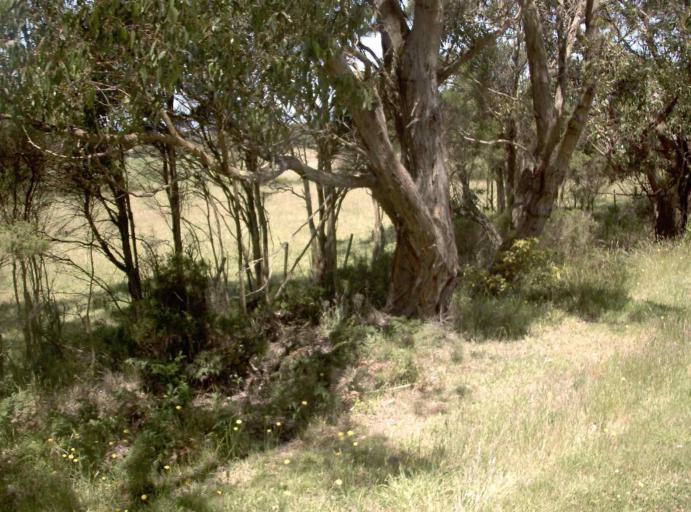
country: AU
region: Victoria
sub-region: Bass Coast
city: North Wonthaggi
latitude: -38.7690
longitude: 146.0647
